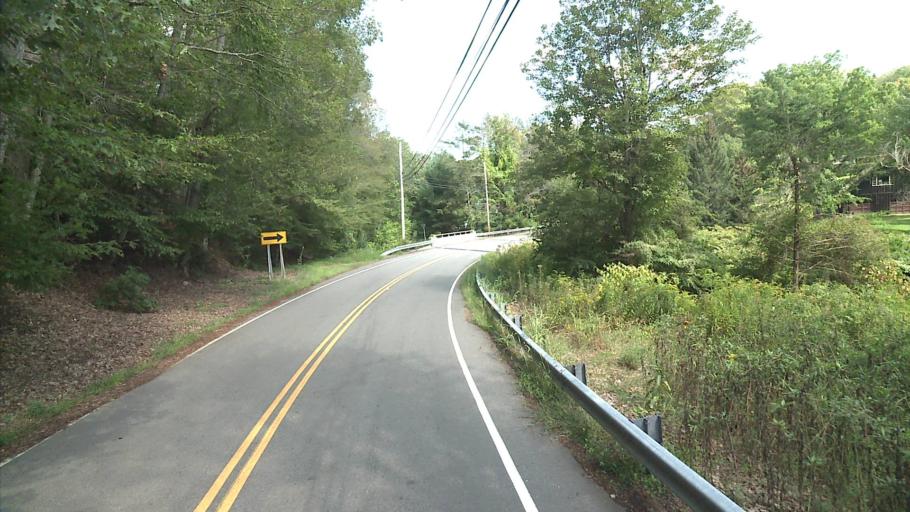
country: US
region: Connecticut
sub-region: Middlesex County
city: Chester Center
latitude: 41.4209
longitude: -72.4137
